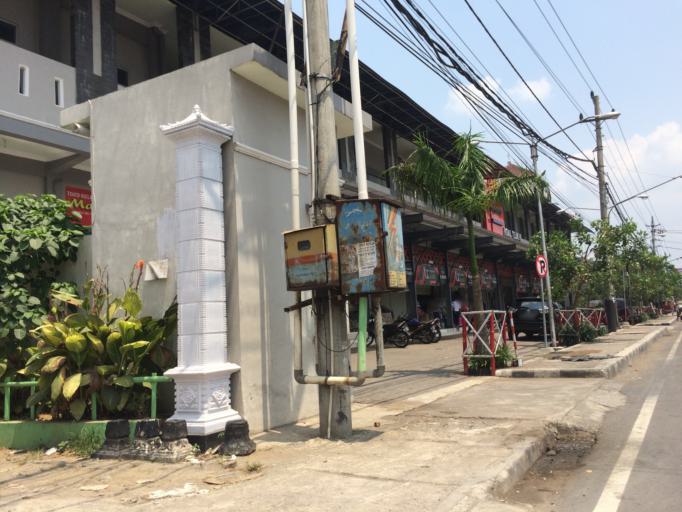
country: ID
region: Central Java
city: Grogol
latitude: -7.6184
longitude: 110.8203
